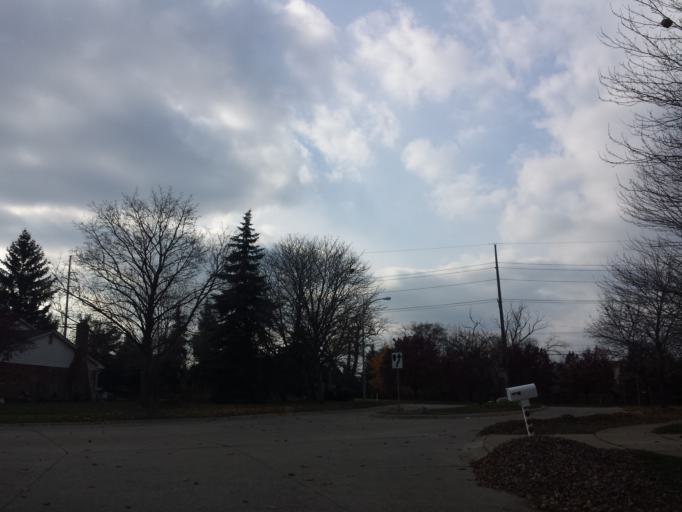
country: US
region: Michigan
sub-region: Wayne County
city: Plymouth
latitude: 42.4081
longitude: -83.4314
